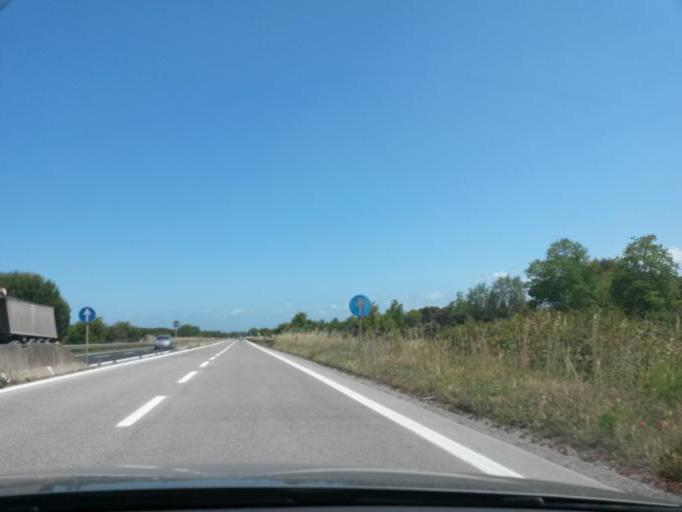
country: IT
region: Tuscany
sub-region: Provincia di Livorno
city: Donoratico
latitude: 43.1328
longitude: 10.5492
